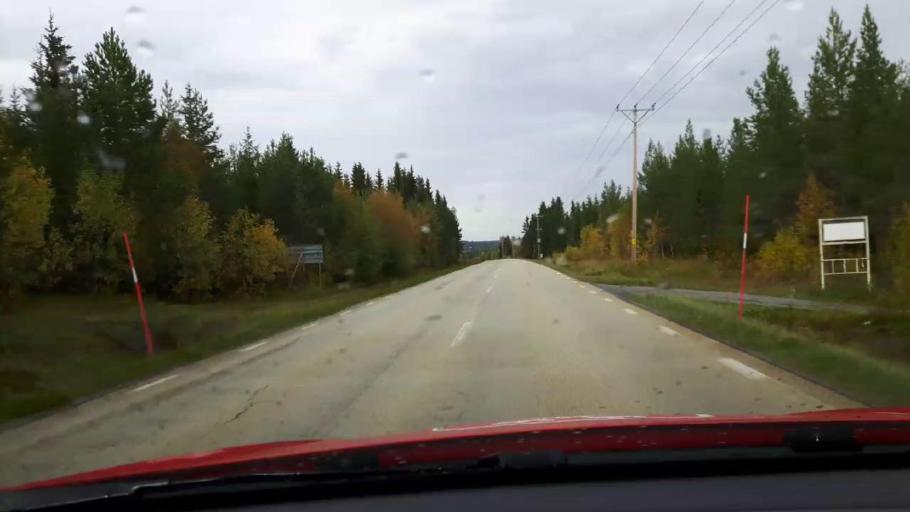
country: SE
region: Jaemtland
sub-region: Bergs Kommun
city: Hoverberg
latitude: 62.9673
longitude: 14.3488
